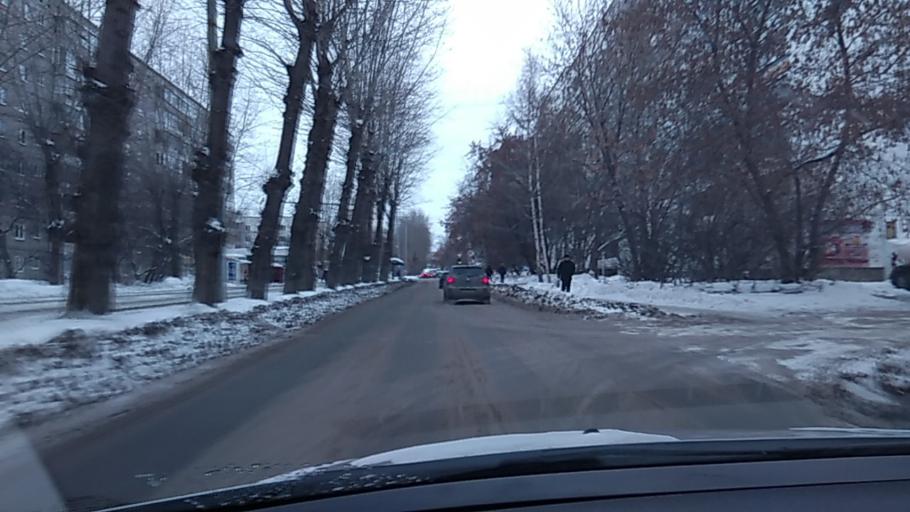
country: RU
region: Sverdlovsk
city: Yekaterinburg
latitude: 56.8221
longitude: 60.6365
